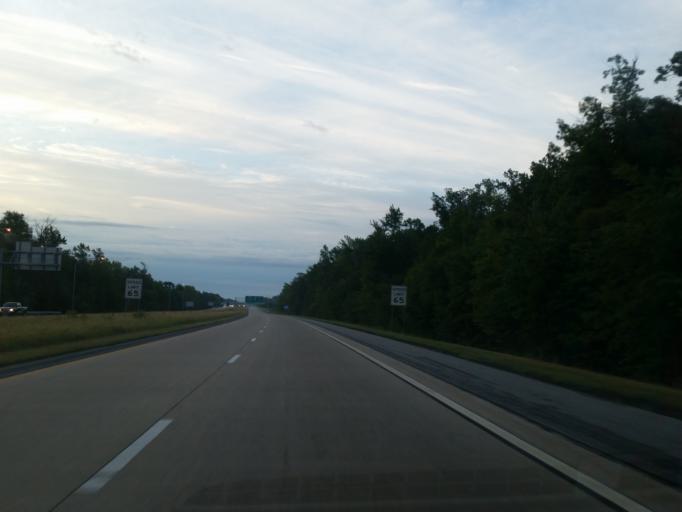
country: US
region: Delaware
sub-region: Kent County
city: Dover
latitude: 39.2003
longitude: -75.5378
